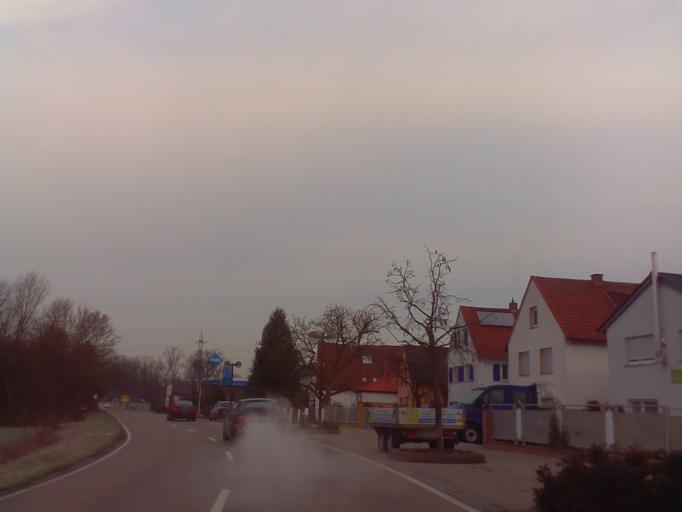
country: DE
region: Rheinland-Pfalz
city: Altrip
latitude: 49.4340
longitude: 8.4856
